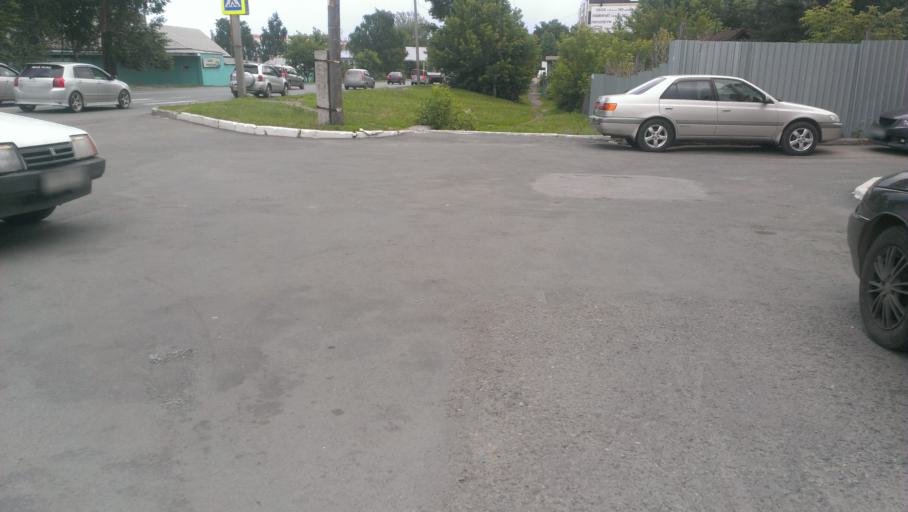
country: RU
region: Altai Krai
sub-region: Gorod Barnaulskiy
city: Barnaul
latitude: 53.3399
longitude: 83.7273
